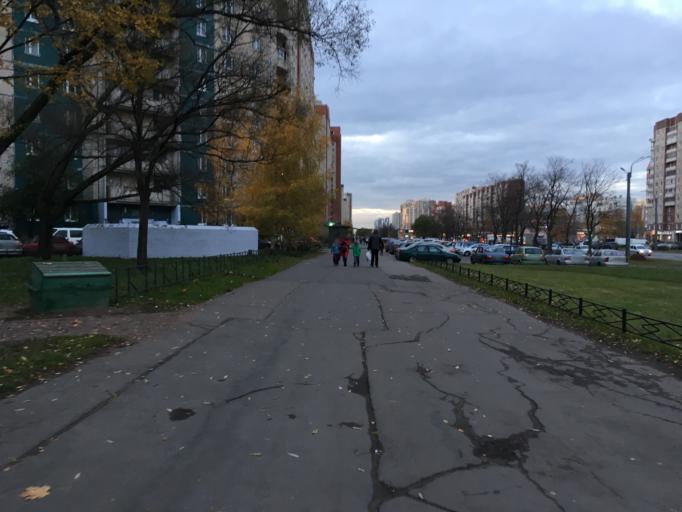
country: RU
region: St.-Petersburg
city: Staraya Derevnya
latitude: 60.0189
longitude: 30.2455
